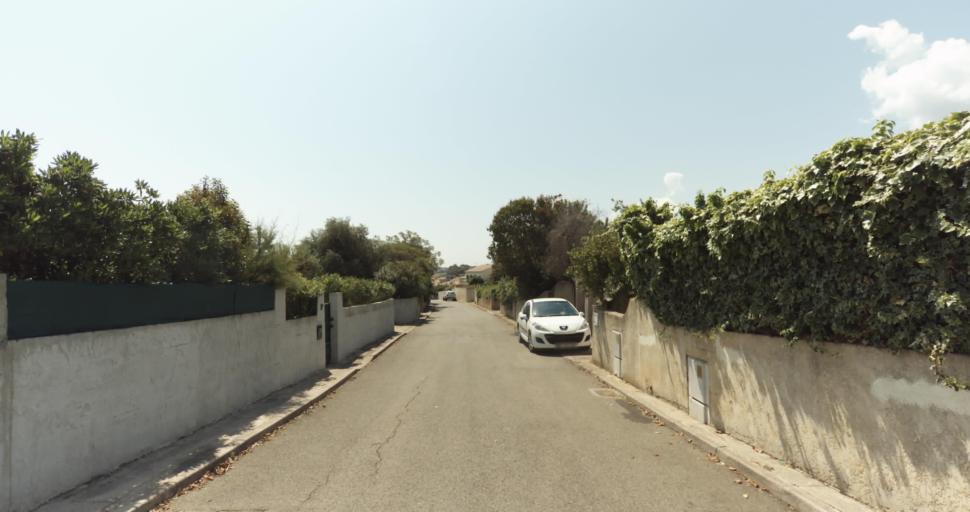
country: FR
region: Corsica
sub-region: Departement de la Haute-Corse
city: Biguglia
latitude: 42.6049
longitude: 9.4316
